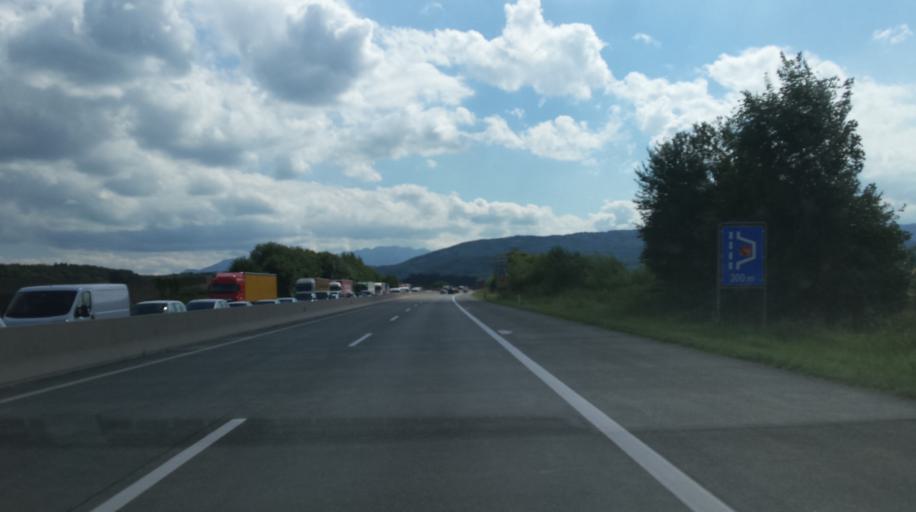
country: AT
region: Upper Austria
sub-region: Politischer Bezirk Vocklabruck
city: Desselbrunn
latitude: 47.9722
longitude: 13.7676
